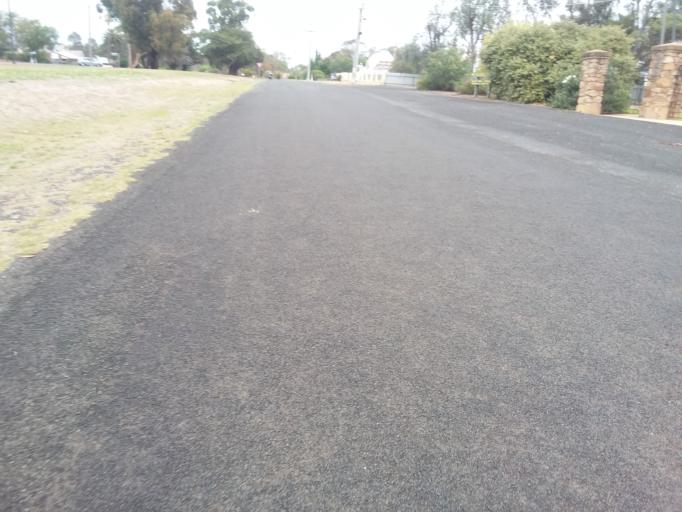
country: AU
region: Victoria
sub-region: Horsham
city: Horsham
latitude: -36.7429
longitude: 141.9378
